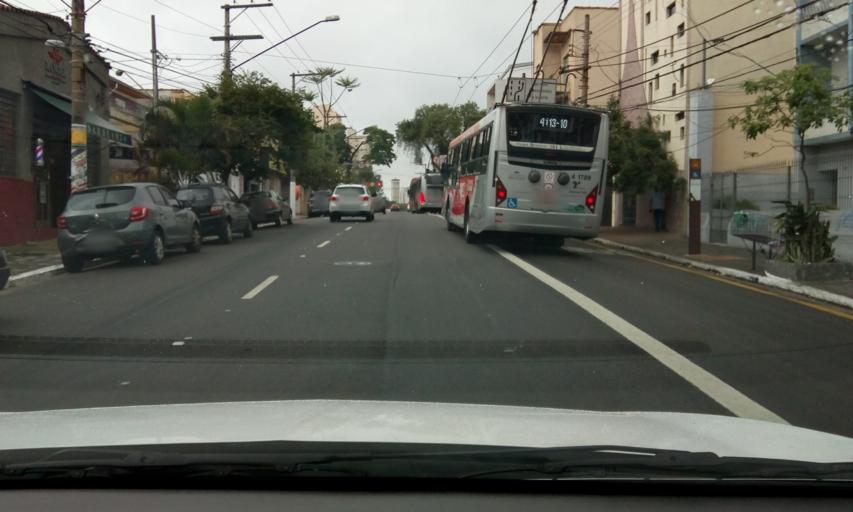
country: BR
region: Sao Paulo
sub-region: Sao Paulo
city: Sao Paulo
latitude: -23.5754
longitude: -46.6249
